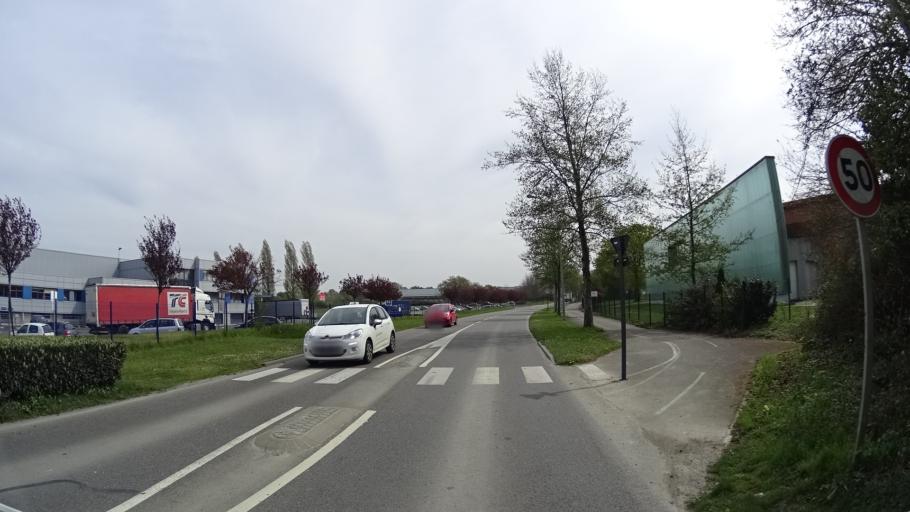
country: FR
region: Brittany
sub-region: Departement d'Ille-et-Vilaine
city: Bruz
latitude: 48.0343
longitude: -1.7366
